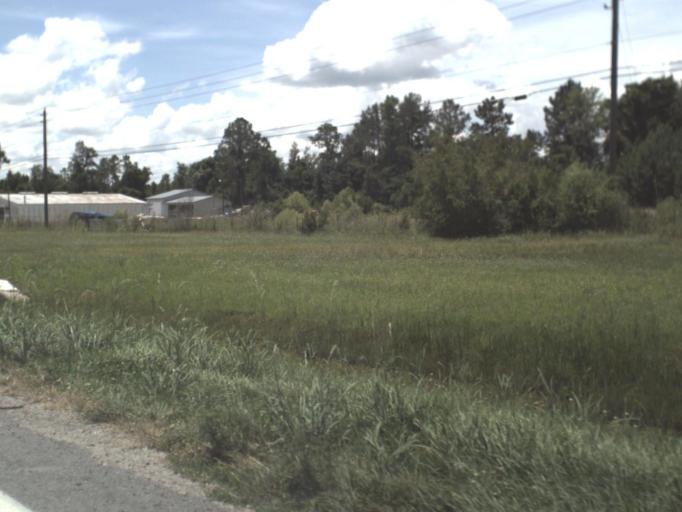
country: US
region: Florida
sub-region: Columbia County
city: Five Points
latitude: 30.2092
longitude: -82.6492
